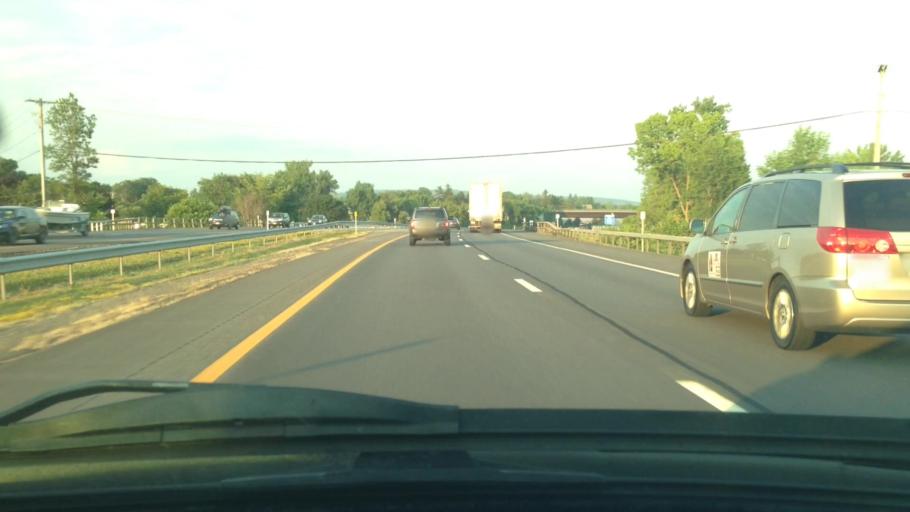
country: US
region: New York
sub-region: Oneida County
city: Whitesboro
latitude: 43.1370
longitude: -75.2777
